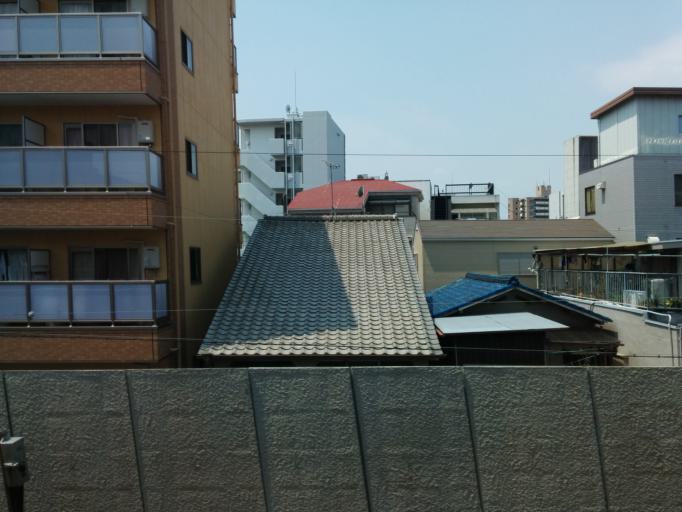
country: JP
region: Osaka
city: Osaka-shi
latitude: 34.7160
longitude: 135.5121
